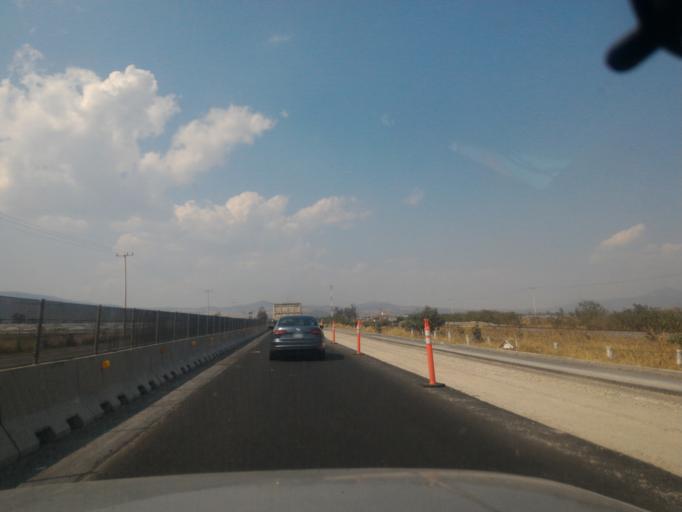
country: MX
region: Jalisco
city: Ciudad Guzman
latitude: 19.7241
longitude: -103.5074
